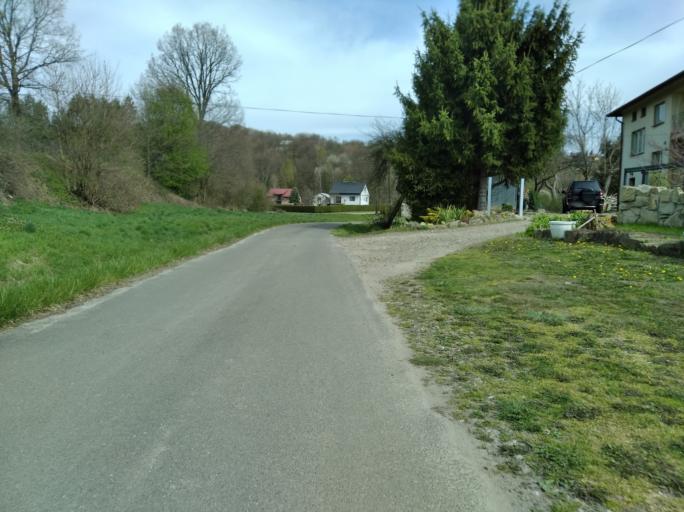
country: PL
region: Subcarpathian Voivodeship
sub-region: Powiat strzyzowski
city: Wisniowa
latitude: 49.8738
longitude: 21.6652
